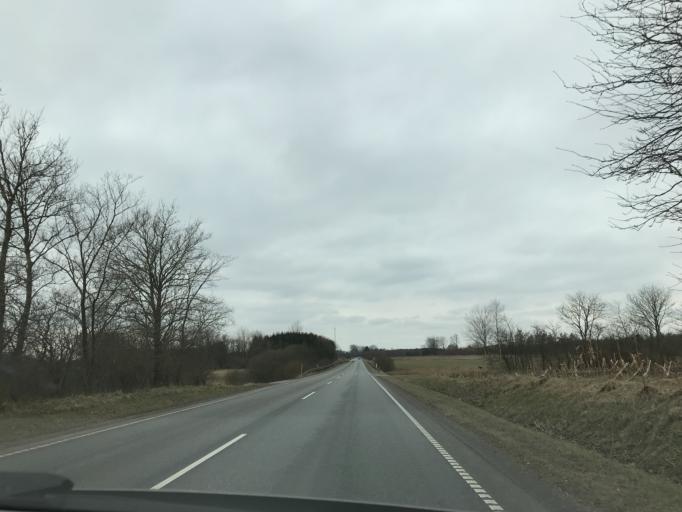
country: DK
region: South Denmark
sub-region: Varde Kommune
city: Olgod
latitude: 55.8170
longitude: 8.6756
